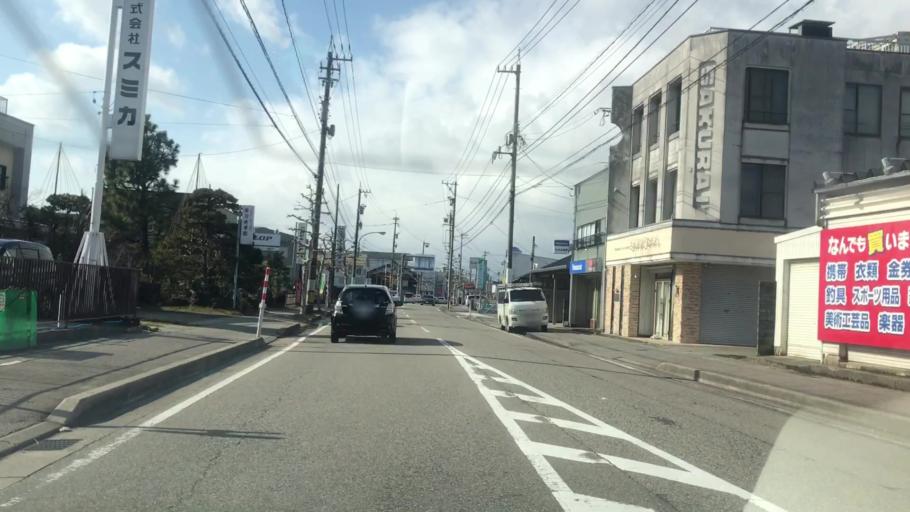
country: JP
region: Toyama
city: Takaoka
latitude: 36.7372
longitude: 137.0317
